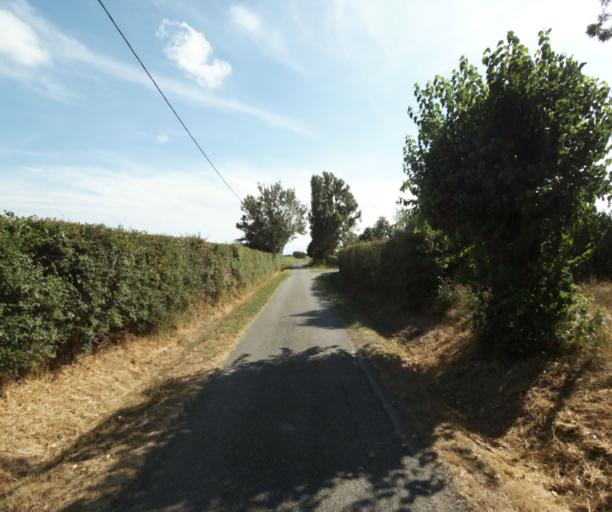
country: FR
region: Midi-Pyrenees
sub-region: Departement de la Haute-Garonne
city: Revel
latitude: 43.5157
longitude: 1.9853
